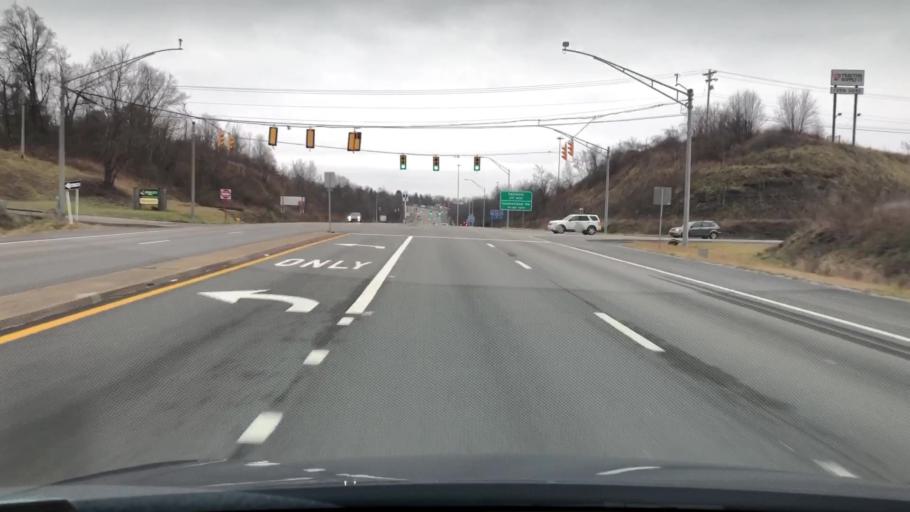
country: US
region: West Virginia
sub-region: Monongalia County
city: Morgantown
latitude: 39.5881
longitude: -79.9550
